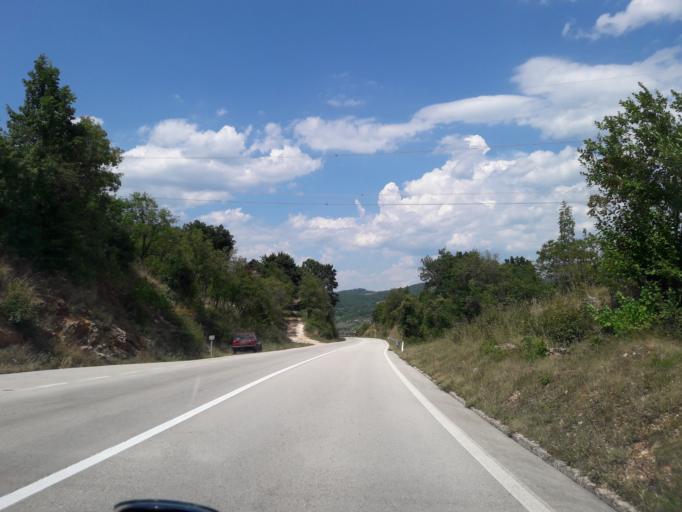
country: BA
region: Republika Srpska
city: Mrkonjic Grad
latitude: 44.5173
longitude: 17.1505
